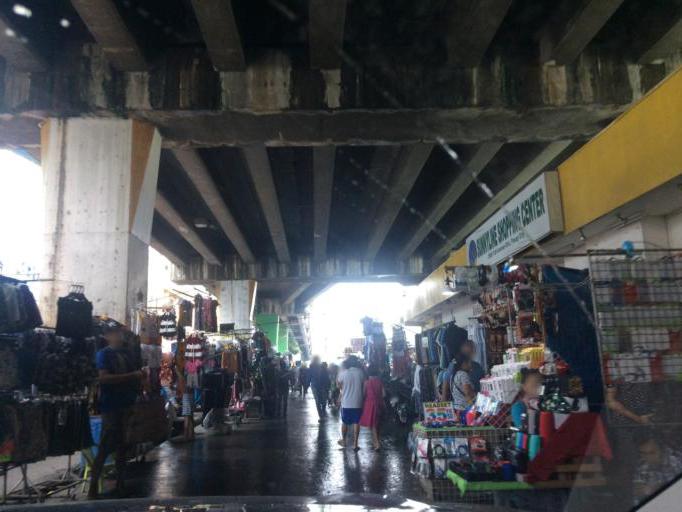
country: PH
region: Metro Manila
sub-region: Makati City
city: Makati City
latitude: 14.5349
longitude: 120.9988
